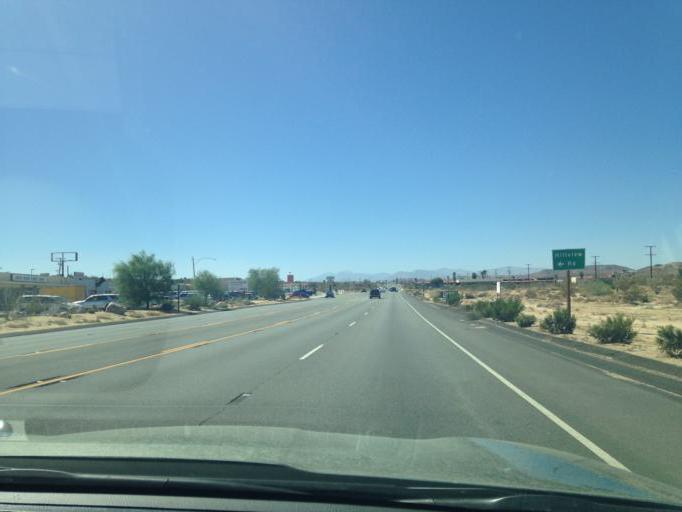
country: US
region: California
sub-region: San Bernardino County
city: Joshua Tree
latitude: 34.1350
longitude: -116.3183
